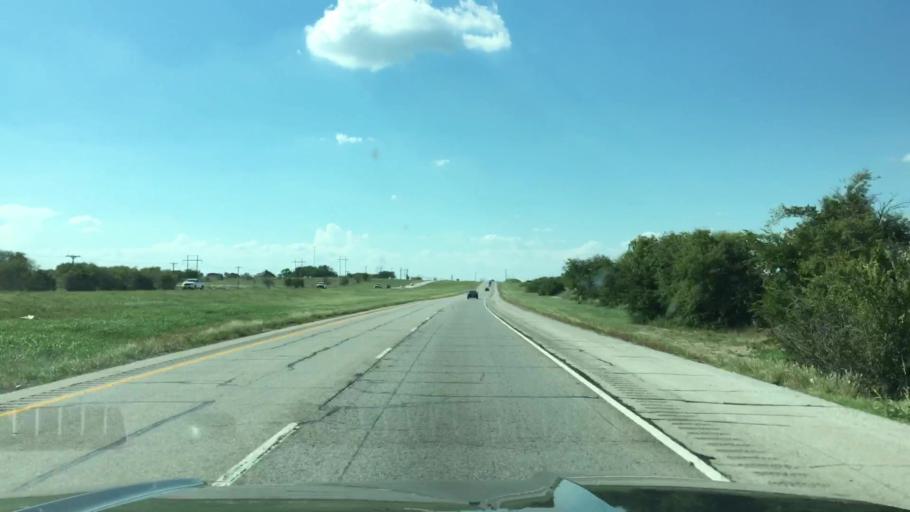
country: US
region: Texas
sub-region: Wise County
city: Decatur
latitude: 33.1640
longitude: -97.5287
